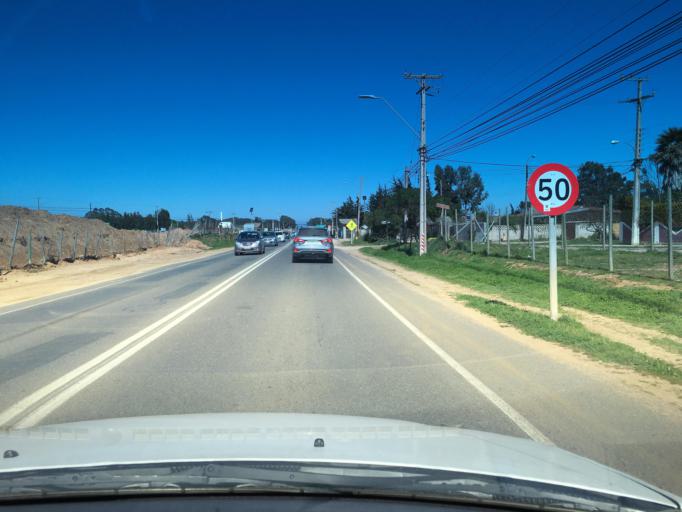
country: CL
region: Valparaiso
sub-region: San Antonio Province
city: El Tabo
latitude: -33.4314
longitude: -71.6880
